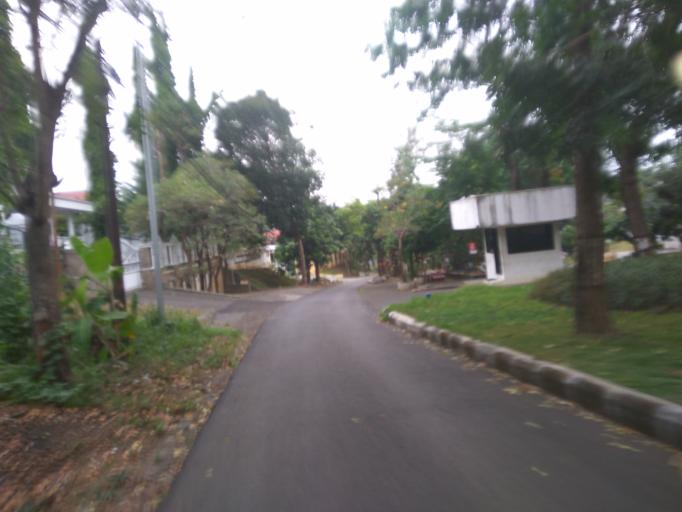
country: ID
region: Central Java
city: Semarang
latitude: -7.0086
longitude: 110.4134
